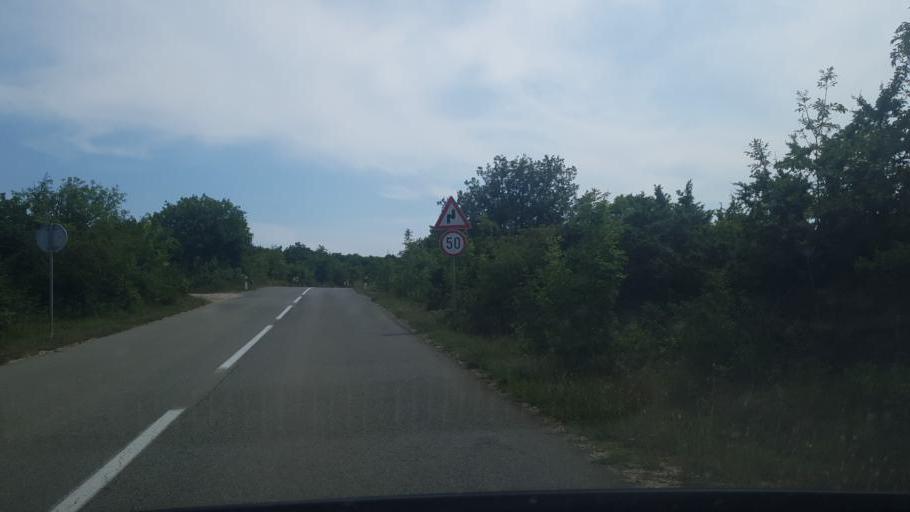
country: HR
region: Primorsko-Goranska
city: Punat
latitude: 45.0540
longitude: 14.6495
